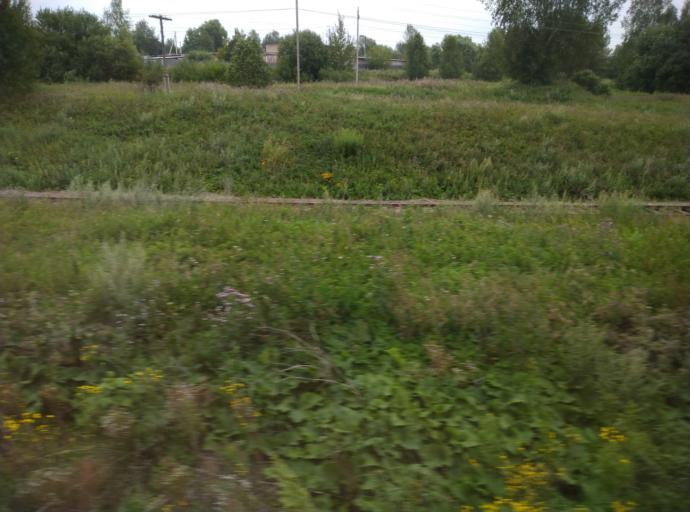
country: RU
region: Kostroma
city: Kosmynino
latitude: 57.5817
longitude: 40.7510
